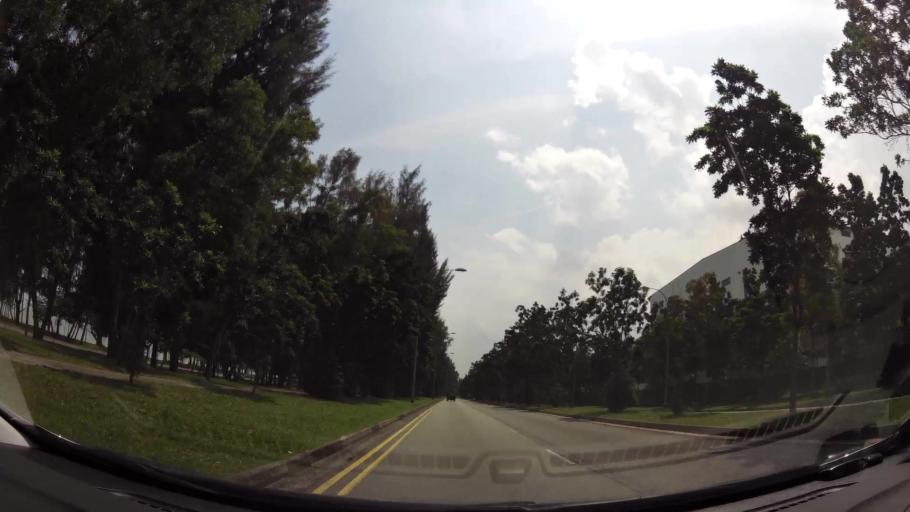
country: MY
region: Johor
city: Kampung Pasir Gudang Baru
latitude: 1.3787
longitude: 104.0028
